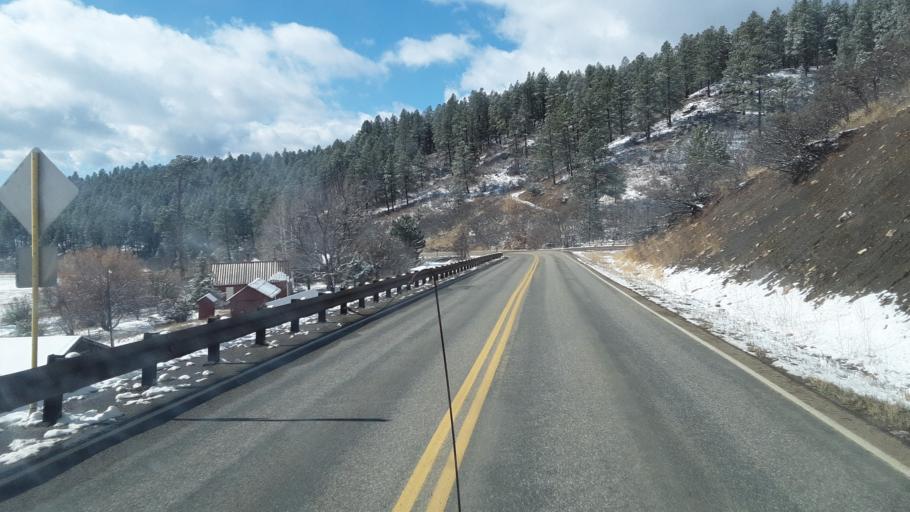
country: US
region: Colorado
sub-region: La Plata County
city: Durango
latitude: 37.3332
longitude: -107.7407
